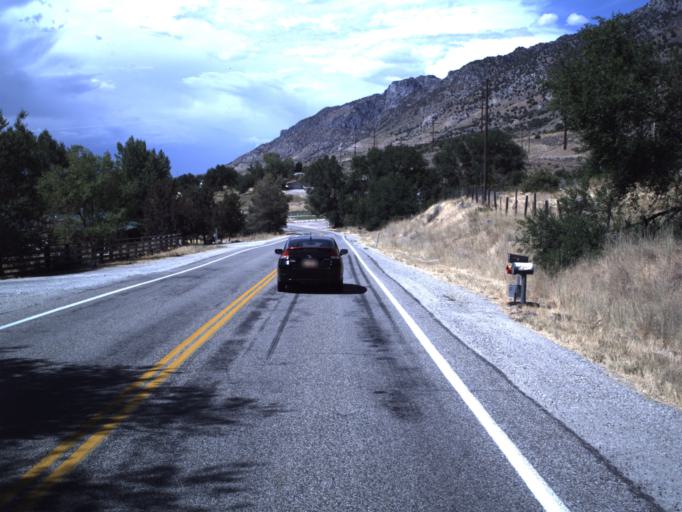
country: US
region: Utah
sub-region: Box Elder County
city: Brigham City
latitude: 41.5629
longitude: -112.0239
